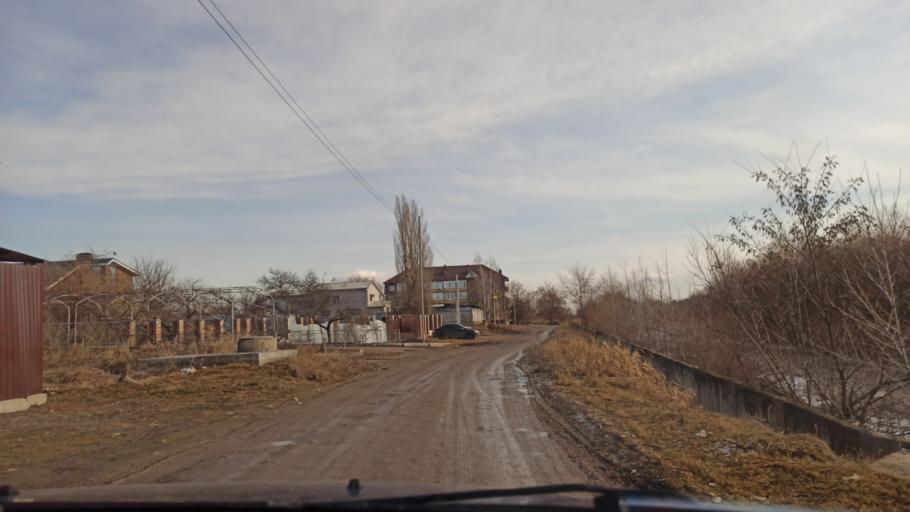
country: RU
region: Stavropol'skiy
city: Yessentukskaya
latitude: 44.0378
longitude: 42.8820
